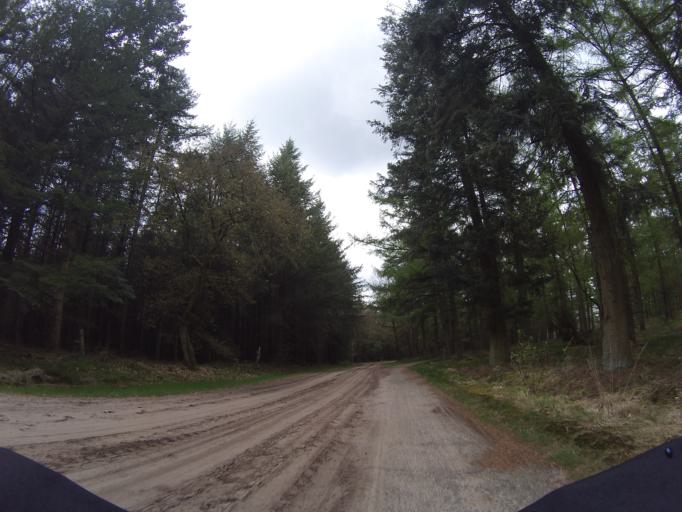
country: NL
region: Overijssel
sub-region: Gemeente Twenterand
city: Magele
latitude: 52.5341
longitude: 6.5440
